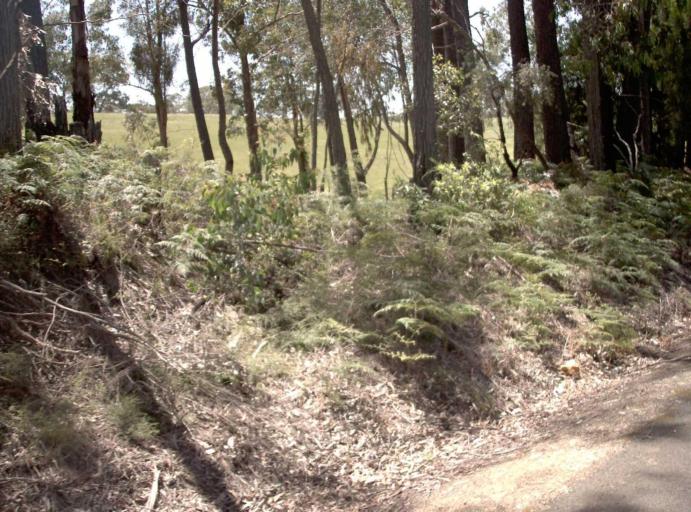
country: AU
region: Victoria
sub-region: East Gippsland
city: Lakes Entrance
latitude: -37.7298
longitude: 148.1302
